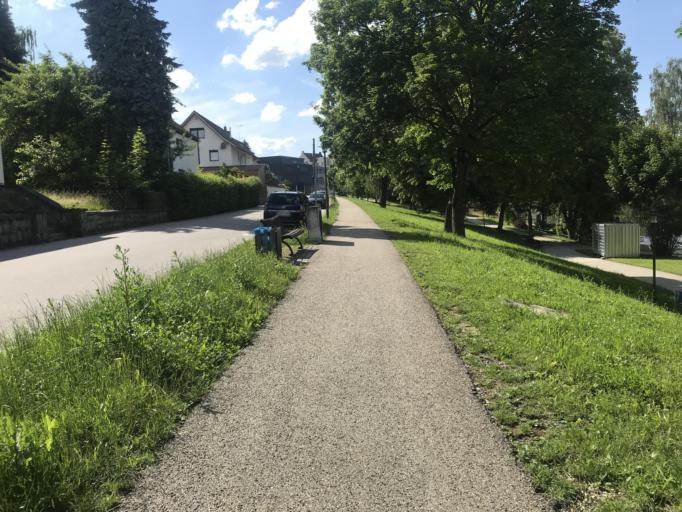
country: DE
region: Bavaria
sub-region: Lower Bavaria
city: Viechtach
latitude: 49.0770
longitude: 12.8909
